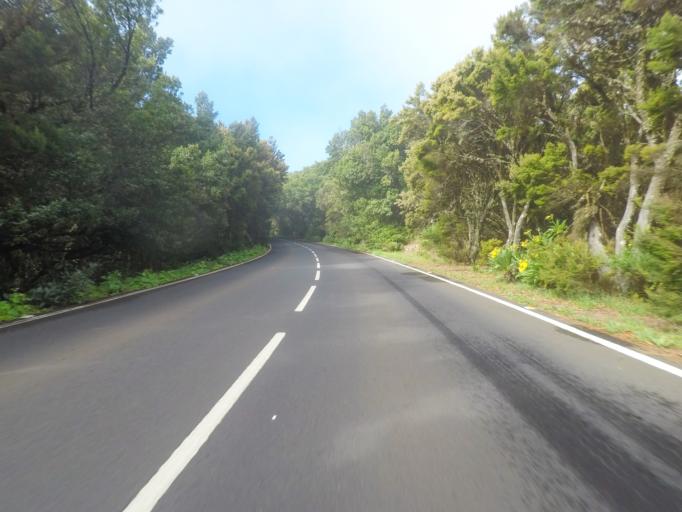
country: ES
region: Canary Islands
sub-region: Provincia de Santa Cruz de Tenerife
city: Alajero
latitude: 28.1093
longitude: -17.2275
